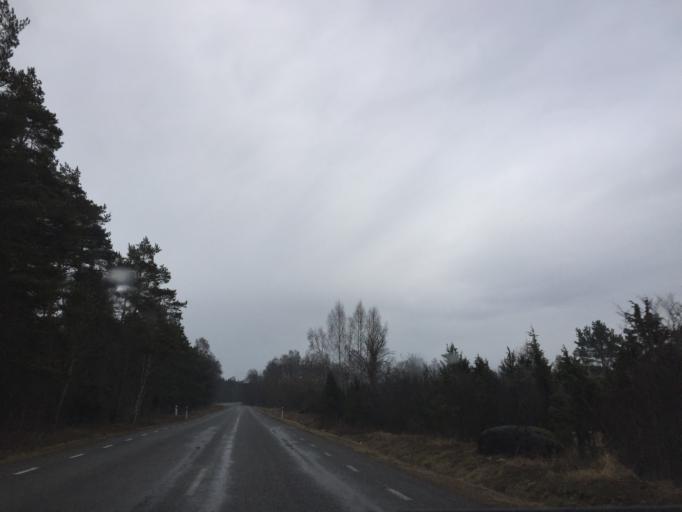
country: EE
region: Saare
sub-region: Orissaare vald
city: Orissaare
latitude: 58.6041
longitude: 22.9717
